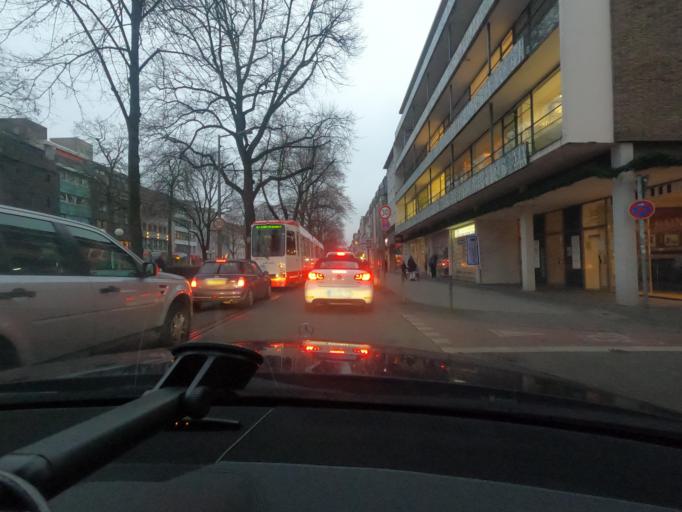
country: DE
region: North Rhine-Westphalia
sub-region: Regierungsbezirk Dusseldorf
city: Krefeld
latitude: 51.3297
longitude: 6.5674
